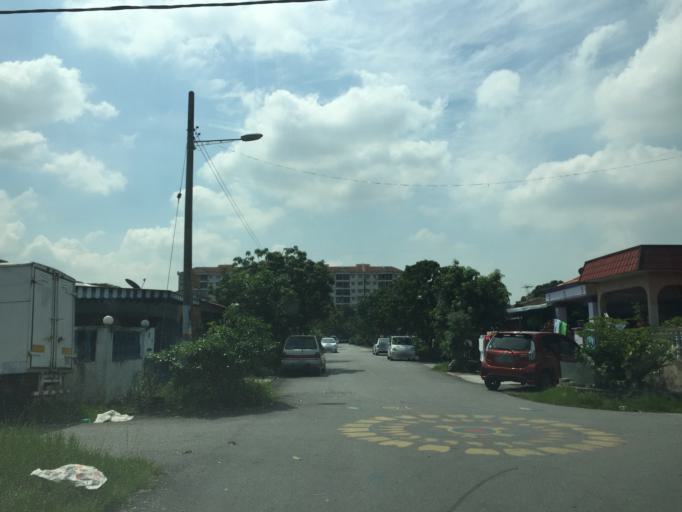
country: MY
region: Selangor
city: Klang
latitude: 3.0076
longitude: 101.4688
